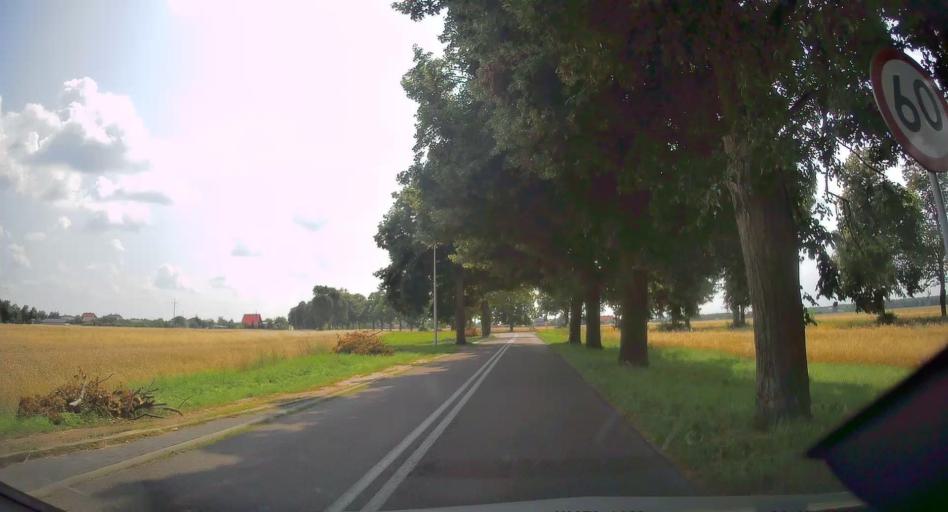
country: PL
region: Lodz Voivodeship
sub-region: Powiat tomaszowski
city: Lubochnia
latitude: 51.5685
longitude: 20.1059
